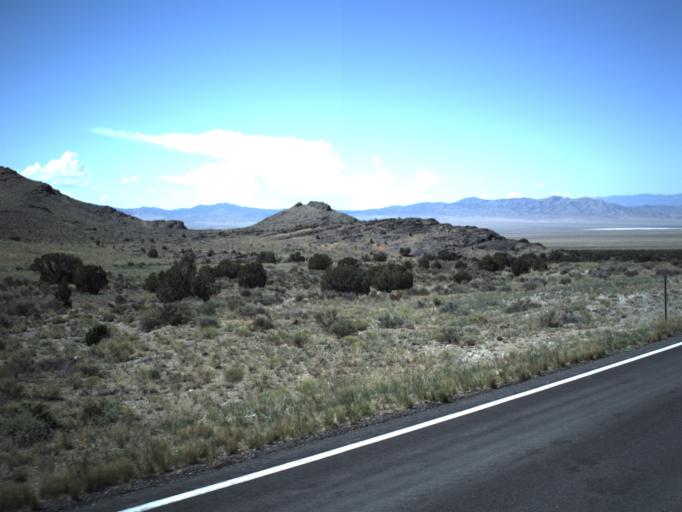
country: US
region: Utah
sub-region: Beaver County
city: Milford
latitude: 39.0789
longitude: -113.7039
